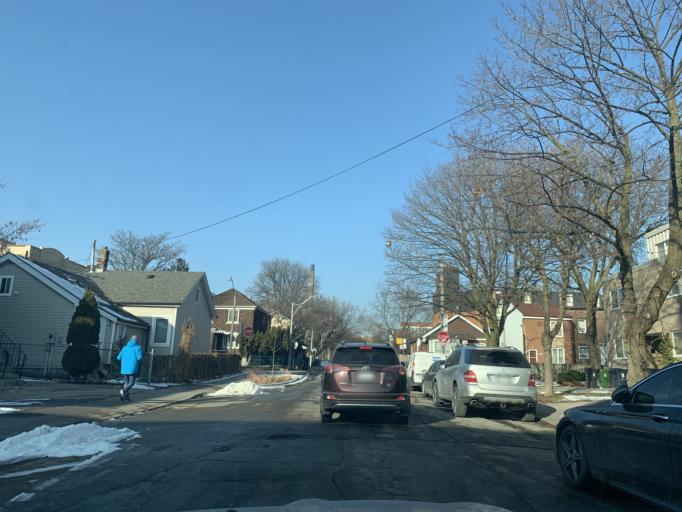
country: CA
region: Ontario
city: Toronto
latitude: 43.6490
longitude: -79.4026
